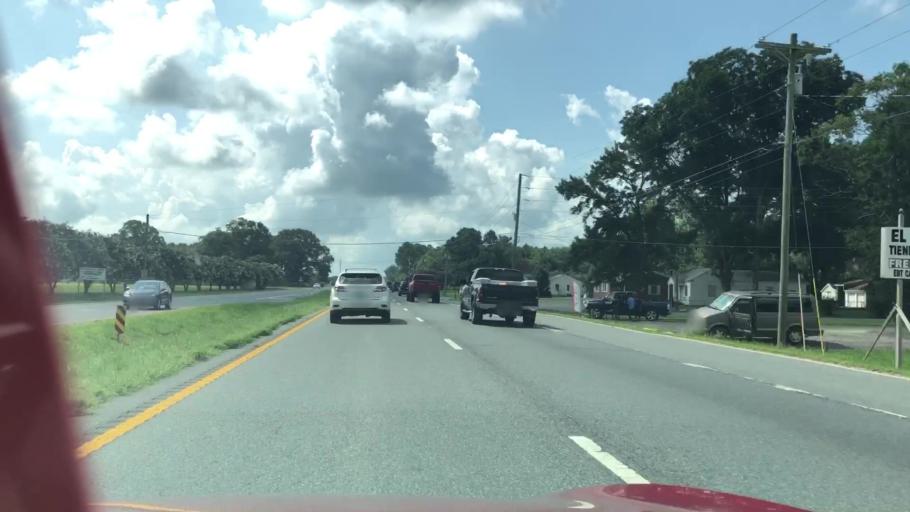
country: US
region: Virginia
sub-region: Accomack County
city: Wattsville
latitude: 37.8720
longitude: -75.5587
